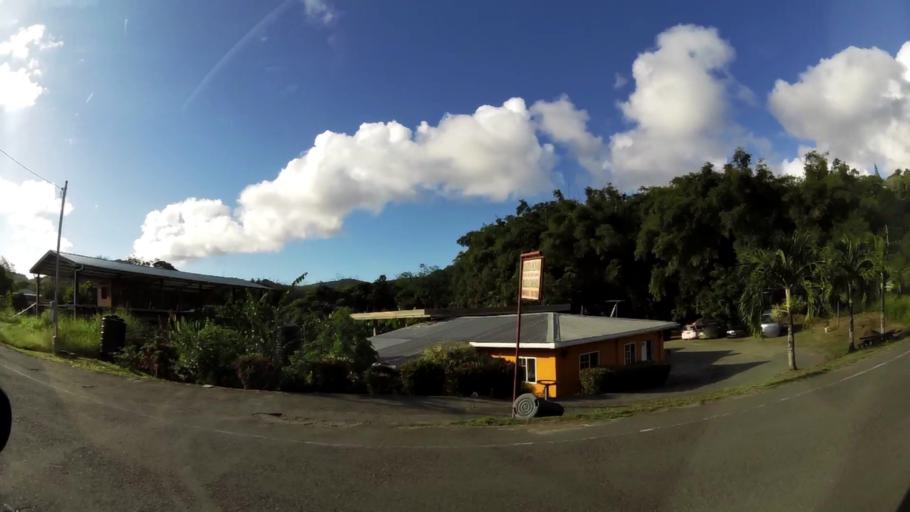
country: TT
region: Eastern Tobago
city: Roxborough
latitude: 11.2262
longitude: -60.6111
